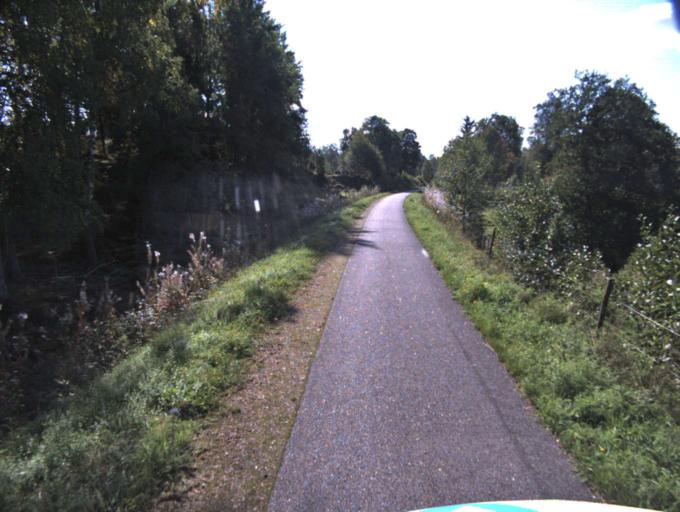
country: SE
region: Vaestra Goetaland
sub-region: Ulricehamns Kommun
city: Ulricehamn
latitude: 57.8377
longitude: 13.2660
